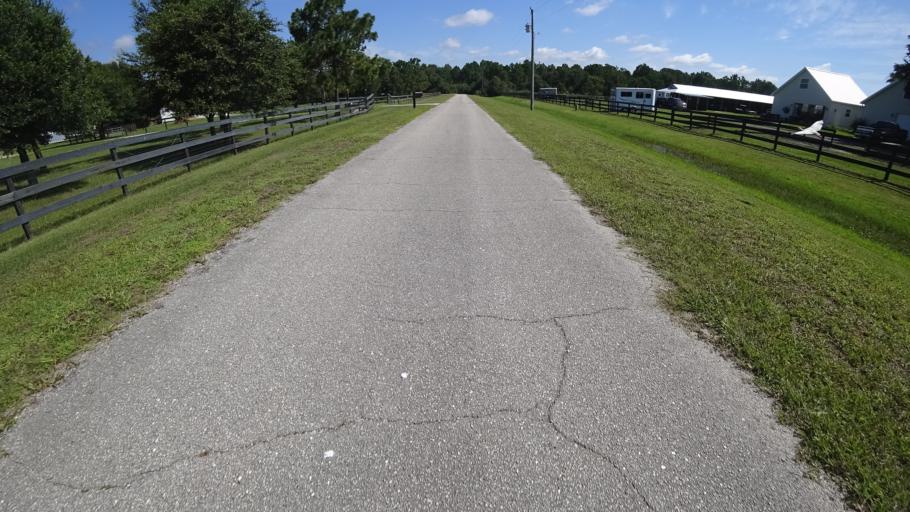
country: US
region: Florida
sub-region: Sarasota County
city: The Meadows
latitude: 27.4206
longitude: -82.3079
